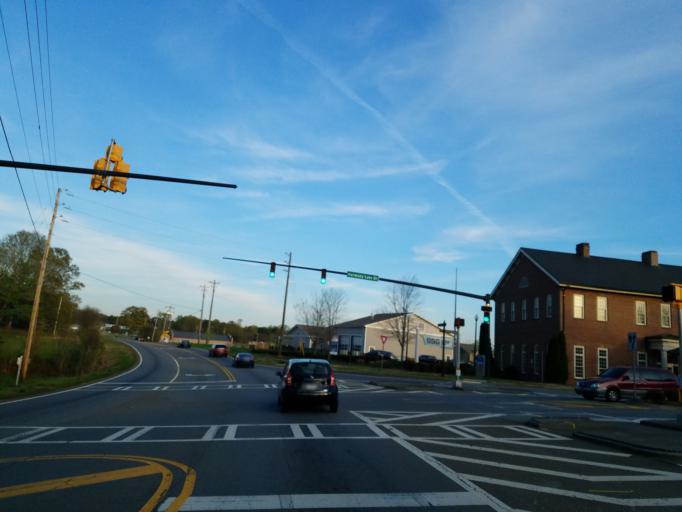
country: US
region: Georgia
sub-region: Cherokee County
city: Holly Springs
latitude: 34.1952
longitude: -84.4488
